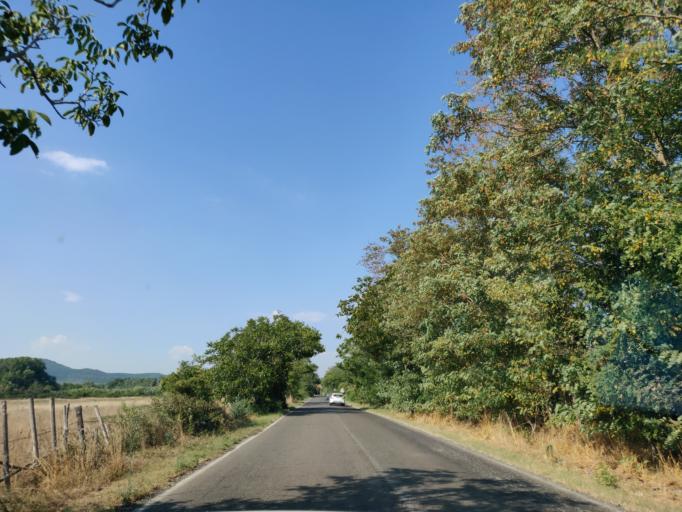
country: IT
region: Latium
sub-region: Provincia di Viterbo
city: Canino
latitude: 42.4099
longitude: 11.6979
